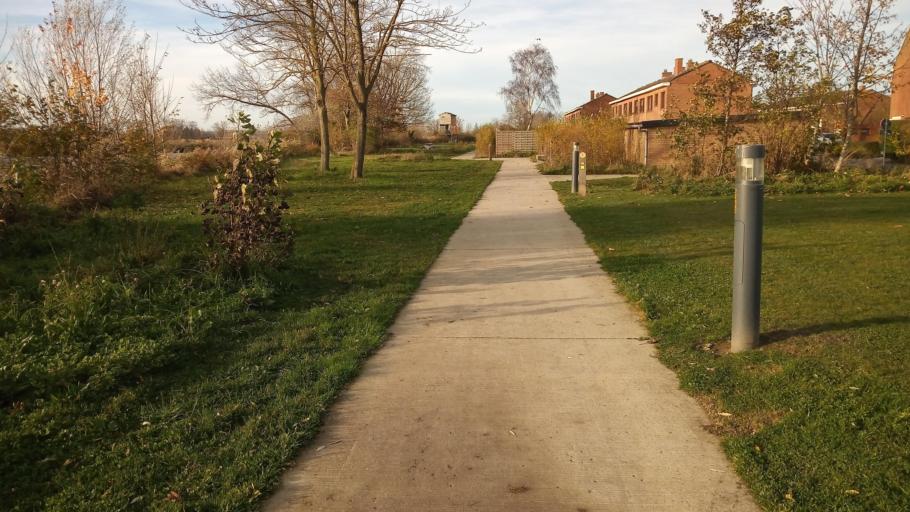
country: BE
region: Flanders
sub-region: Provincie West-Vlaanderen
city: Oudenburg
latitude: 51.1973
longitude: 2.9695
